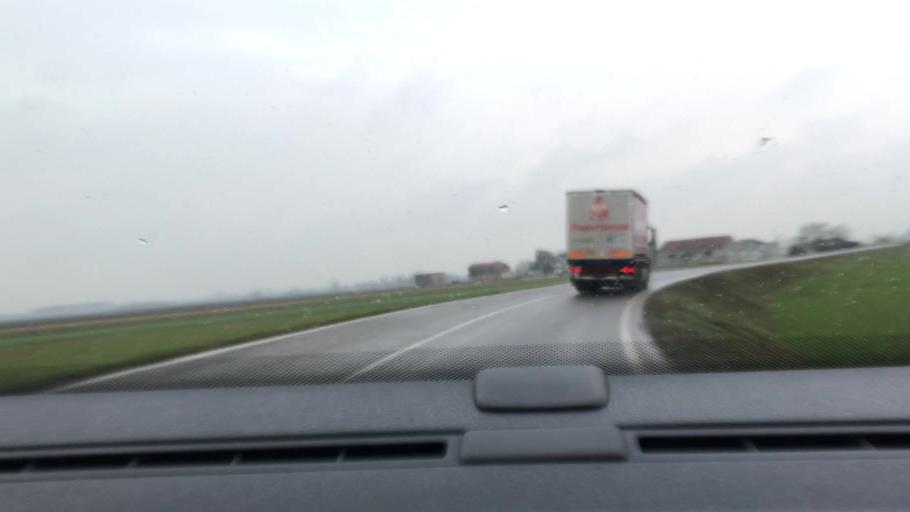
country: IT
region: Lombardy
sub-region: Provincia di Mantova
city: Gazzuolo
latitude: 45.0089
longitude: 10.6045
